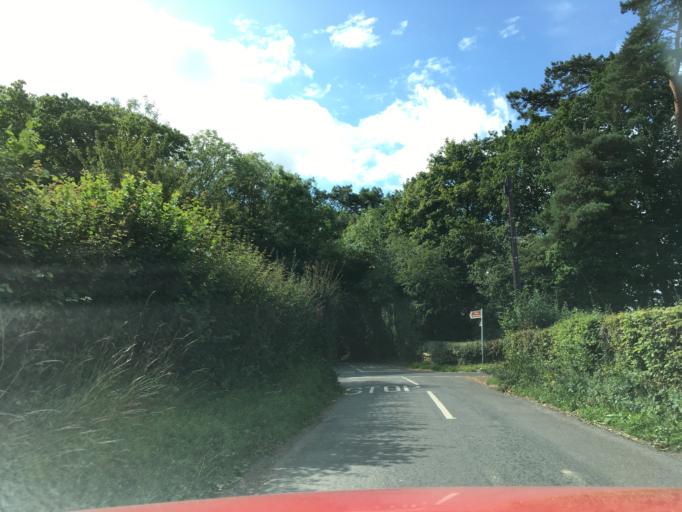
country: GB
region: England
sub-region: Kent
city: Maidstone
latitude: 51.2261
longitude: 0.5511
